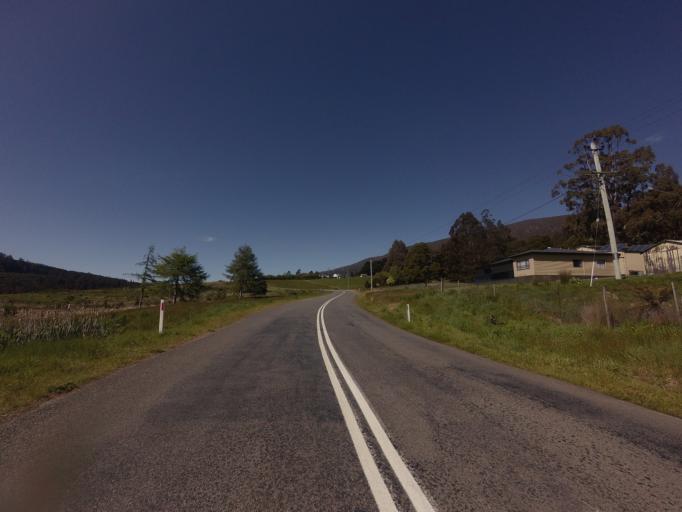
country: AU
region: Tasmania
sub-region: Derwent Valley
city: New Norfolk
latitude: -42.7528
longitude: 146.6344
